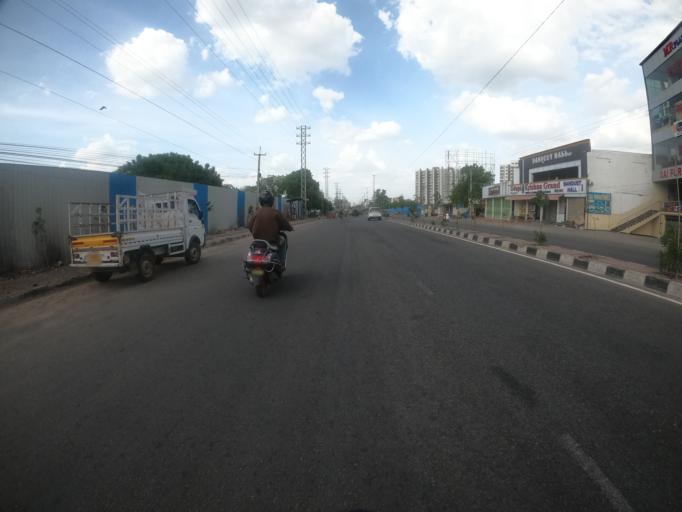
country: IN
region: Telangana
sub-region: Hyderabad
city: Hyderabad
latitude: 17.3558
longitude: 78.3809
